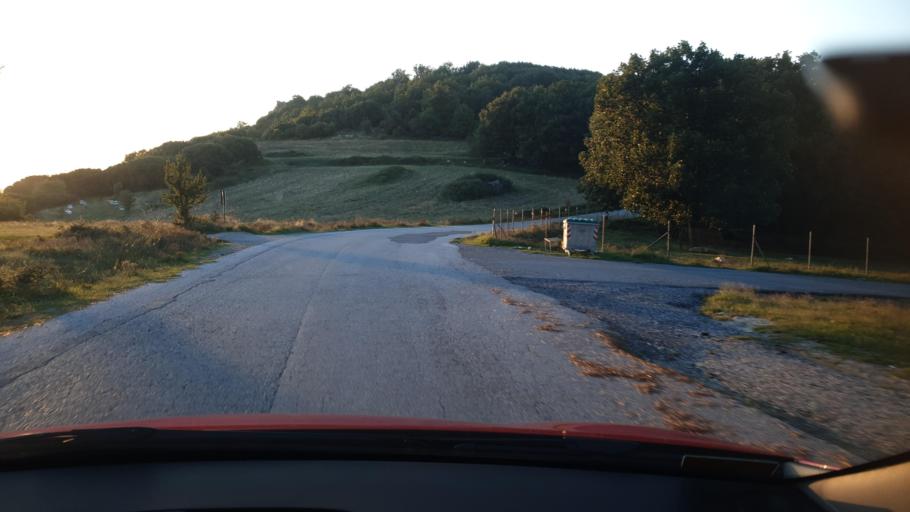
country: GR
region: Central Macedonia
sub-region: Nomos Thessalonikis
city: Peristera
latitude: 40.5132
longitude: 23.2149
